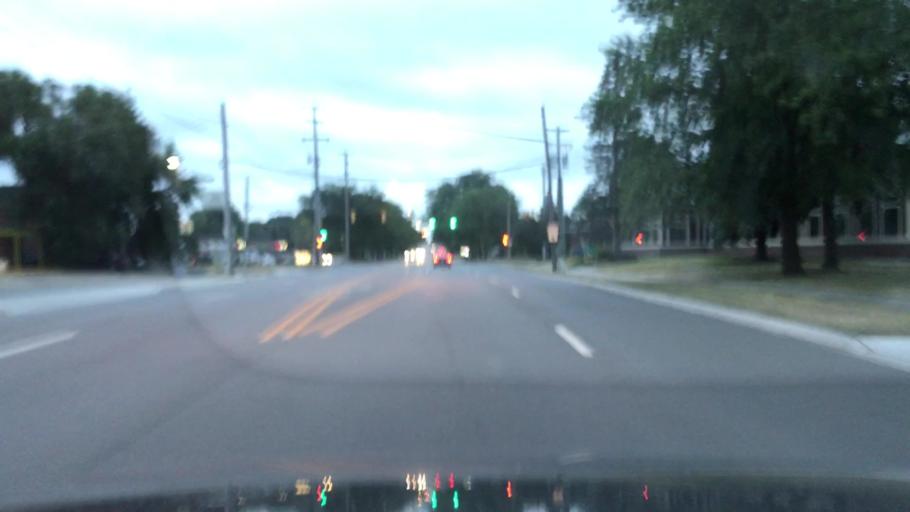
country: US
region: Michigan
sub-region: Kent County
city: Grand Rapids
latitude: 42.9844
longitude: -85.6313
